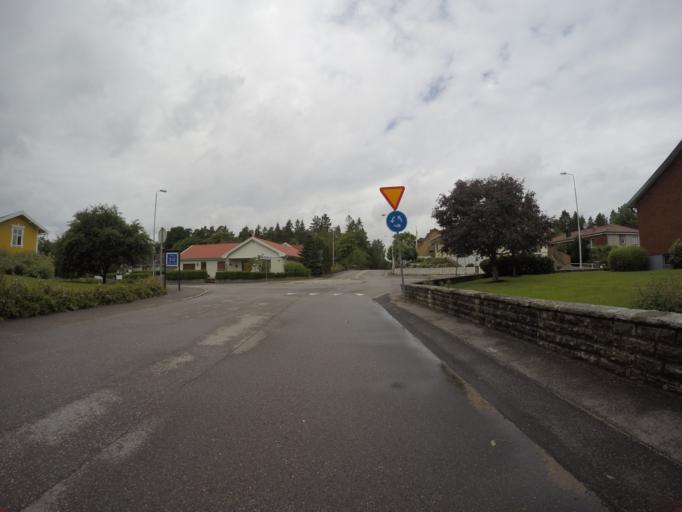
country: SE
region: Vaestra Goetaland
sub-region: Trollhattan
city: Trollhattan
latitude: 58.2652
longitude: 12.2723
